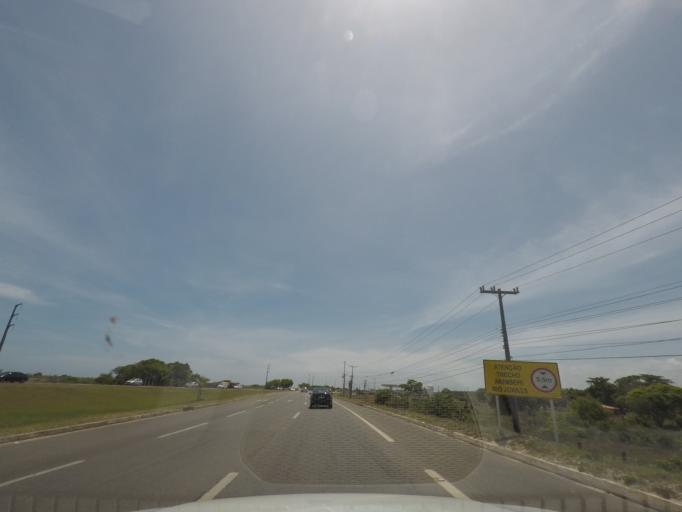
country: BR
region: Bahia
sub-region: Camacari
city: Camacari
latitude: -12.7170
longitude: -38.1528
